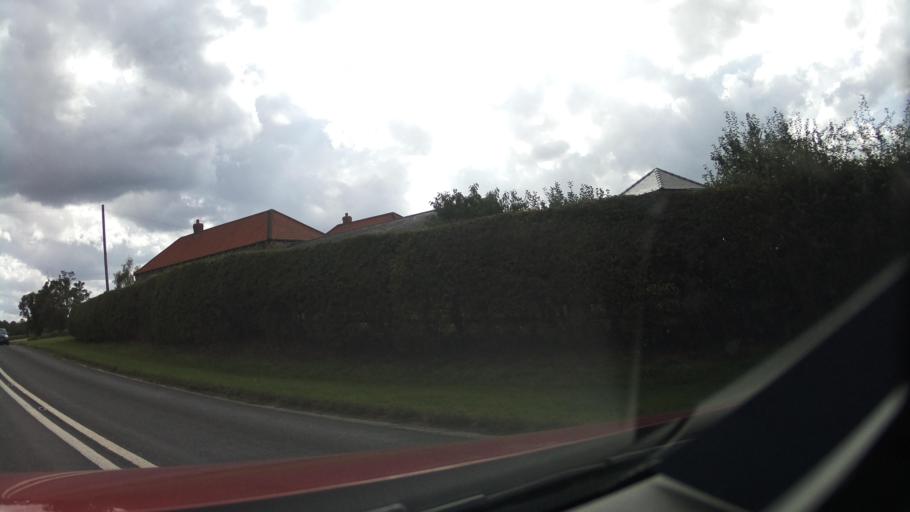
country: GB
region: England
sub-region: North Yorkshire
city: Ripon
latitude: 54.1594
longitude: -1.5415
